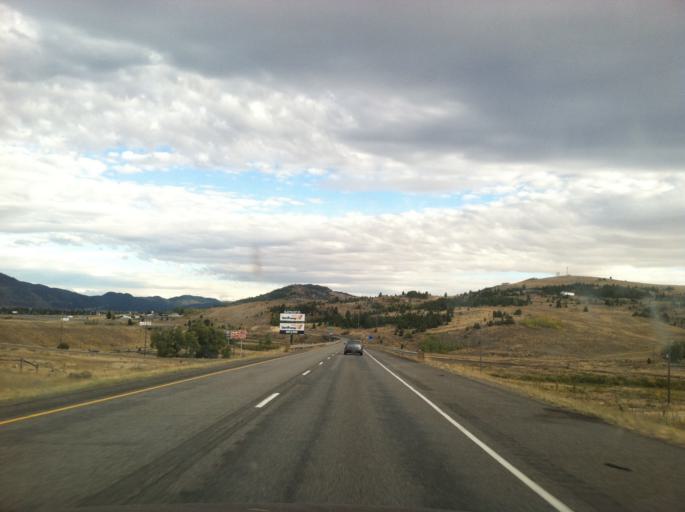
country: US
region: Montana
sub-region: Silver Bow County
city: Butte
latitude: 46.0010
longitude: -112.5700
